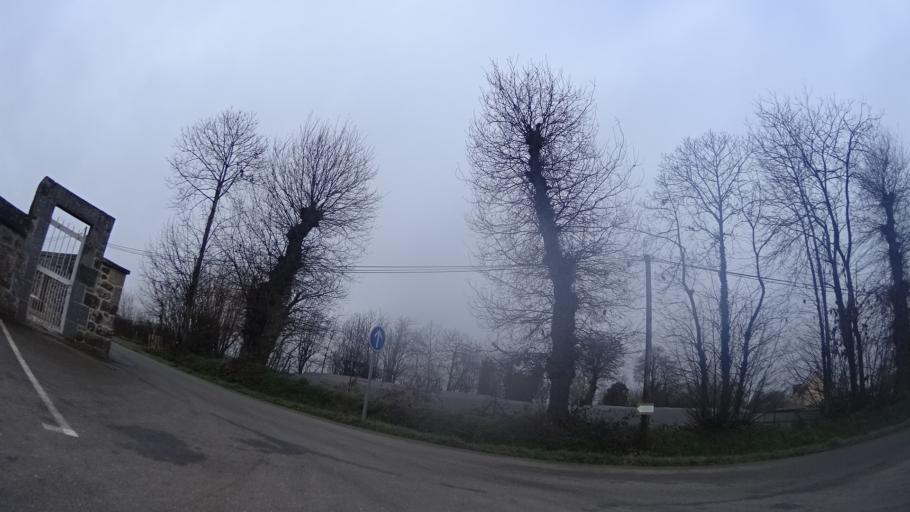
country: FR
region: Brittany
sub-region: Departement des Cotes-d'Armor
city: Evran
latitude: 48.3351
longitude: -1.9368
